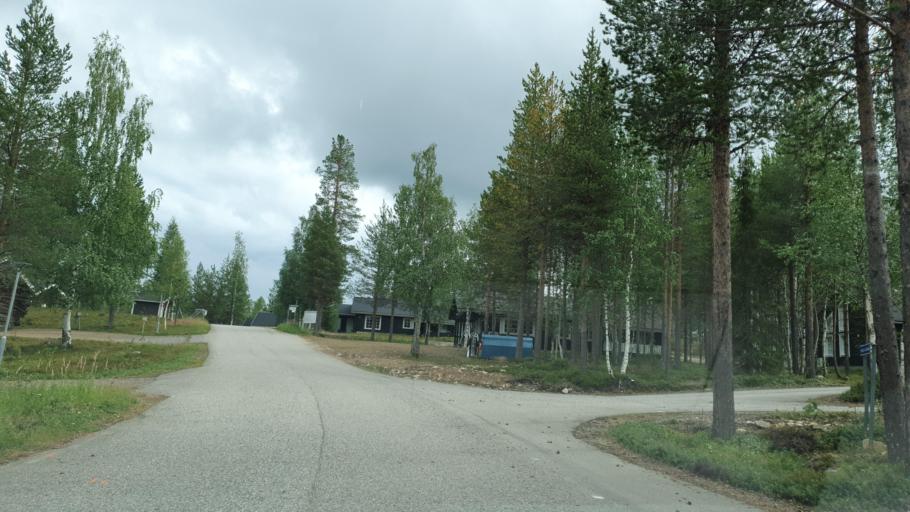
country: FI
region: Lapland
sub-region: Tunturi-Lappi
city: Kolari
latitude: 67.5302
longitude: 24.2577
